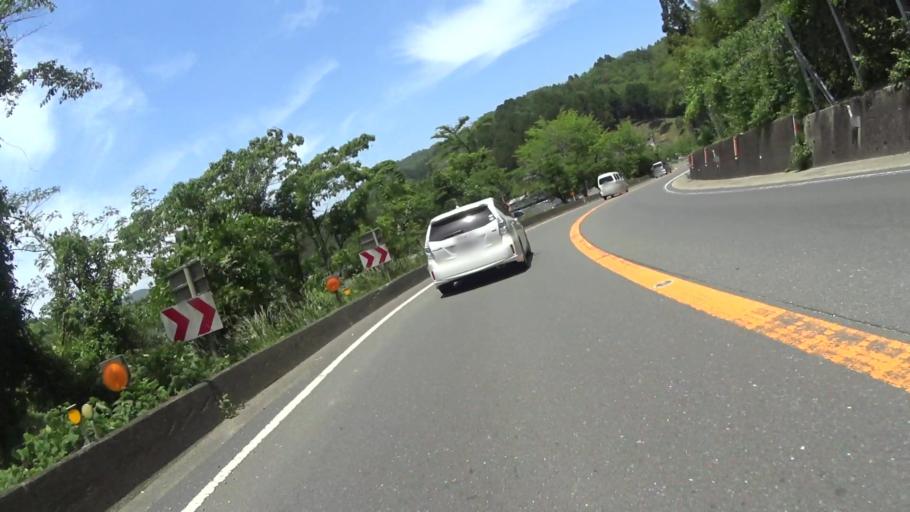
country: JP
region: Kyoto
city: Kameoka
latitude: 35.1274
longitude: 135.4335
